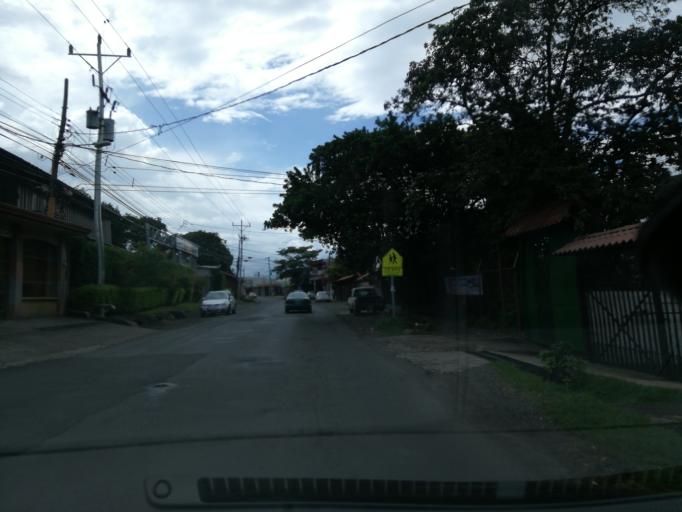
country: CR
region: Alajuela
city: Alajuela
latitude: 9.9960
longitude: -84.2240
